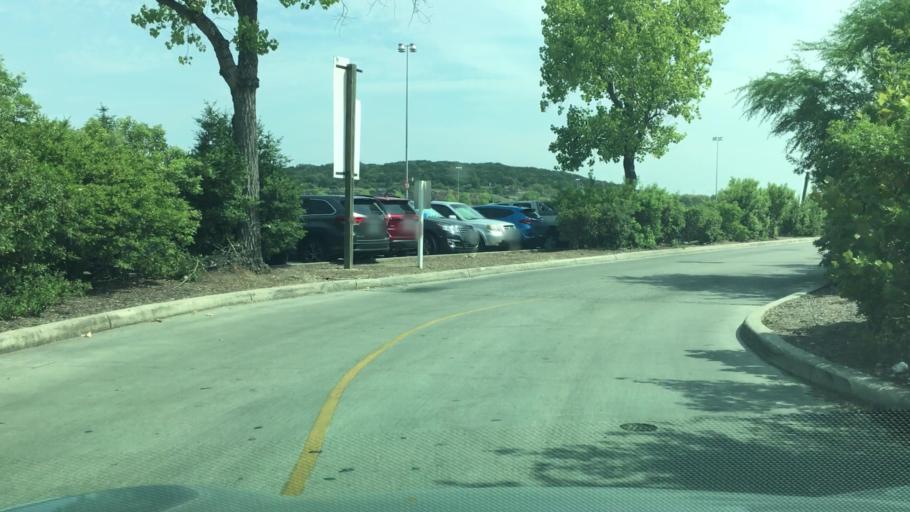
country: US
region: Texas
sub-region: Bexar County
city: Shavano Park
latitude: 29.5991
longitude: -98.6070
